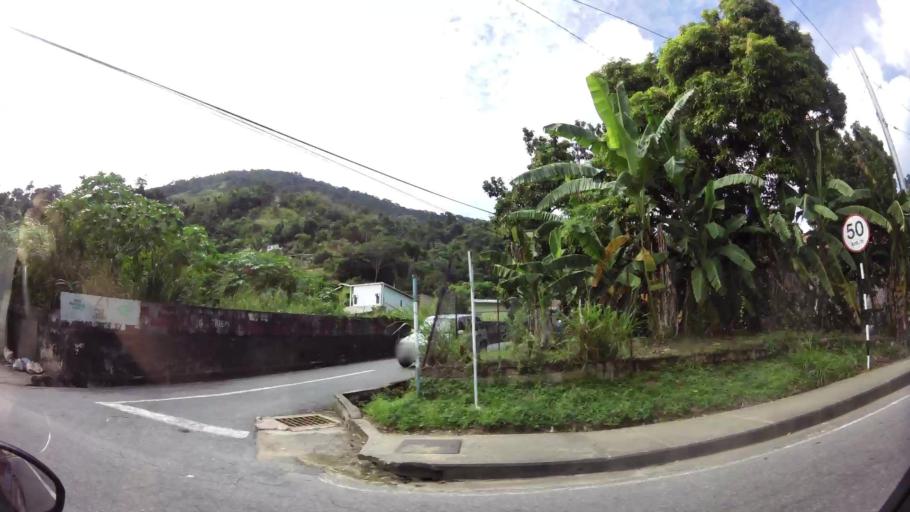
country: TT
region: Diego Martin
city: Petit Valley
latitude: 10.7112
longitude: -61.5604
